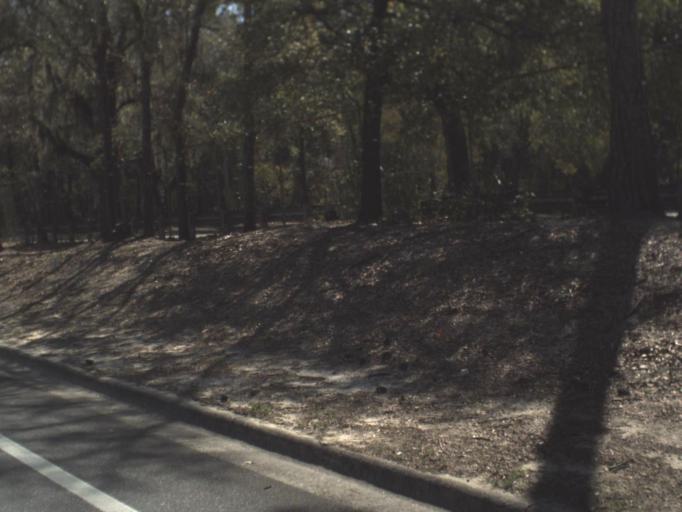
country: US
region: Florida
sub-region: Leon County
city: Tallahassee
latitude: 30.4204
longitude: -84.3508
